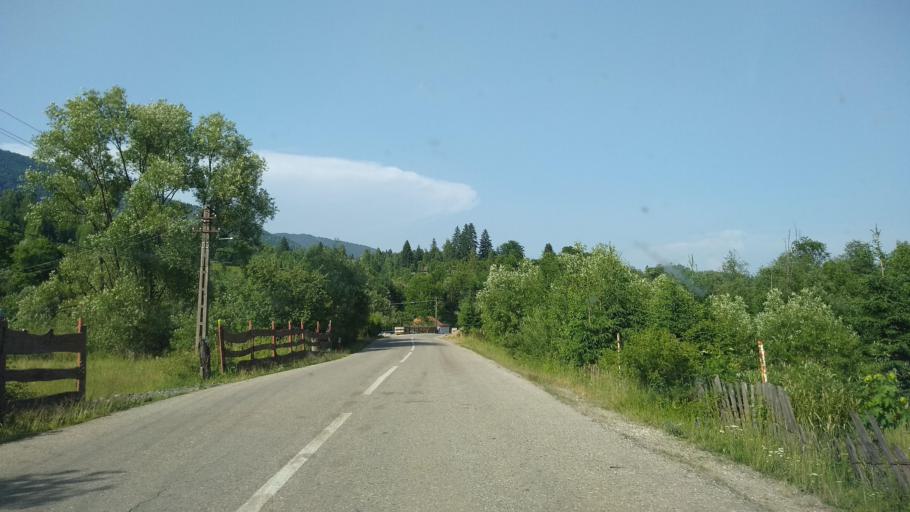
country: RO
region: Hunedoara
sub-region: Comuna Uricani
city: Uricani
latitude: 45.3041
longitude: 23.0266
